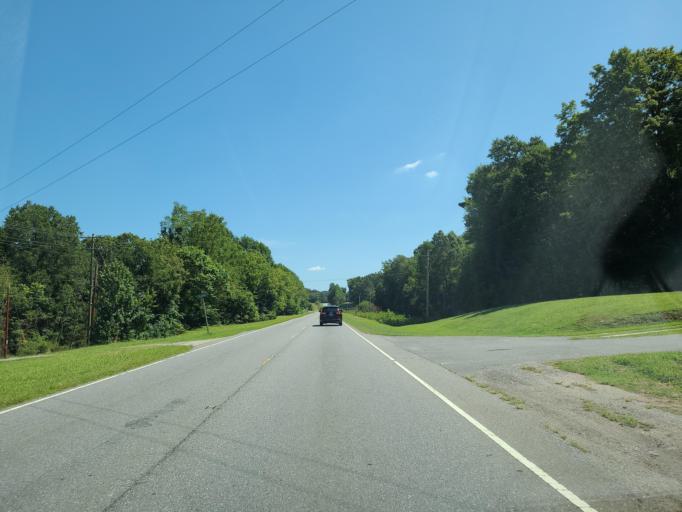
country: US
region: North Carolina
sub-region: Lincoln County
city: Lincolnton
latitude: 35.4508
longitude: -81.2500
